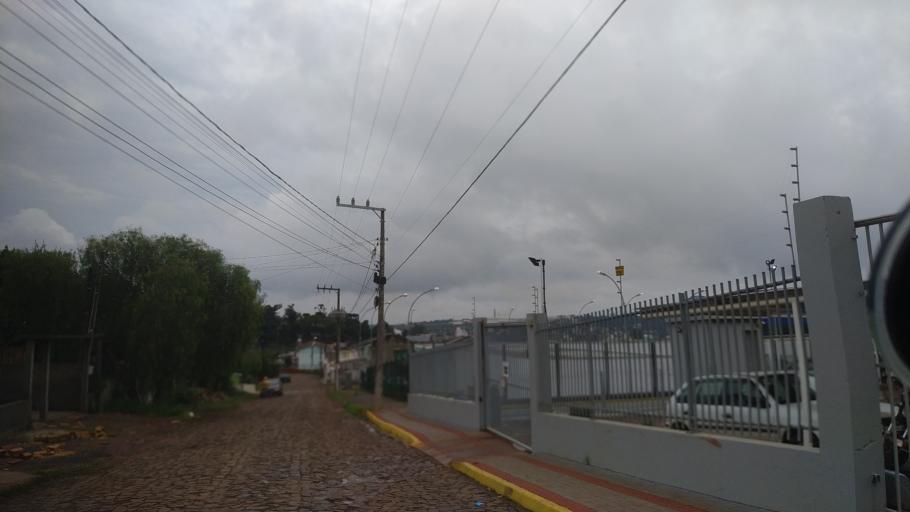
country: BR
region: Santa Catarina
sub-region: Chapeco
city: Chapeco
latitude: -27.1053
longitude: -52.6757
